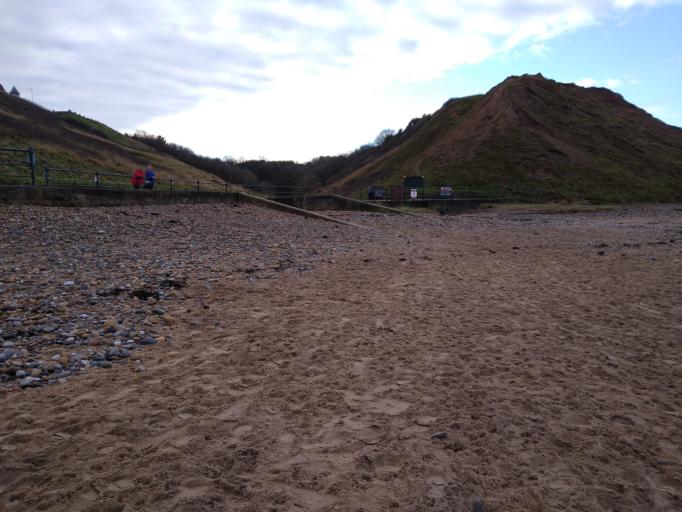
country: GB
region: England
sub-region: Redcar and Cleveland
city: Saltburn-by-the-Sea
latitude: 54.5873
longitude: -0.9758
